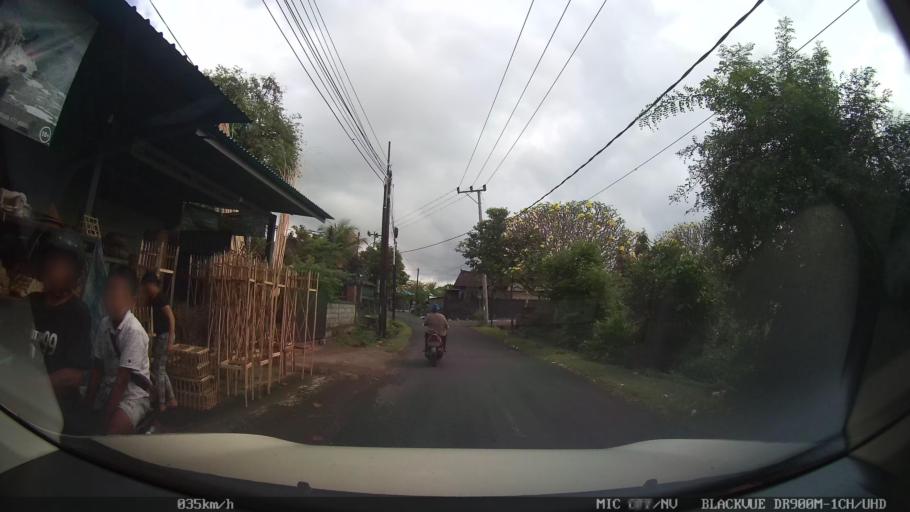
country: ID
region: Bali
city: Banjar Bucu
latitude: -8.5905
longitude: 115.2058
